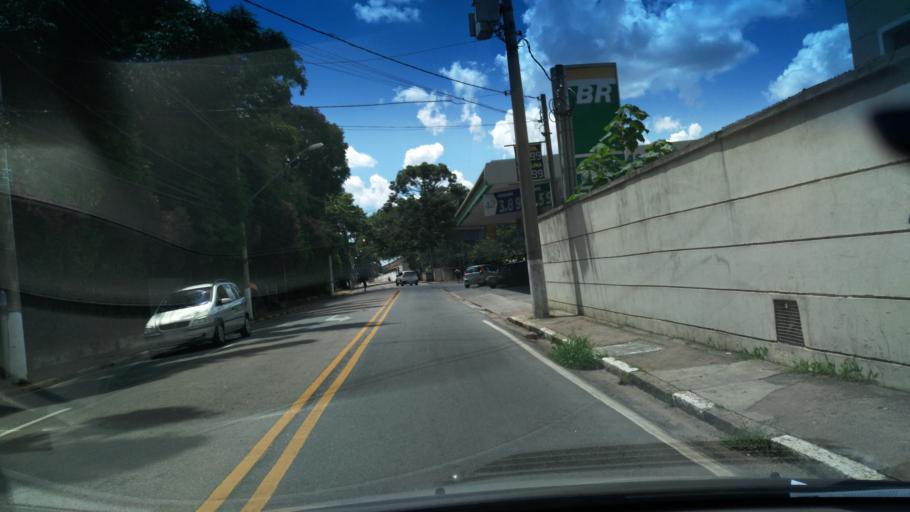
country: BR
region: Sao Paulo
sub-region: Vinhedo
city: Vinhedo
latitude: -23.0176
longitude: -46.9827
